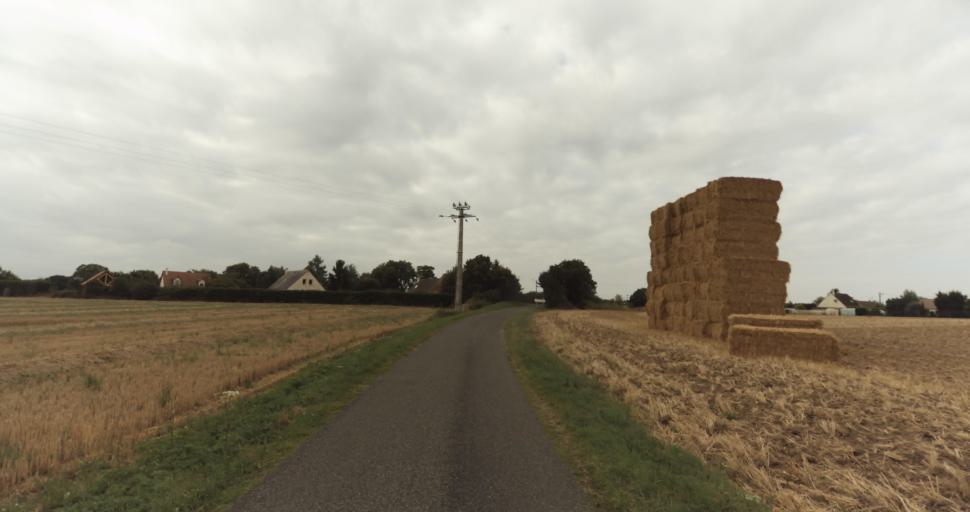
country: FR
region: Haute-Normandie
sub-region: Departement de l'Eure
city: Marcilly-sur-Eure
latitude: 48.8272
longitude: 1.3145
